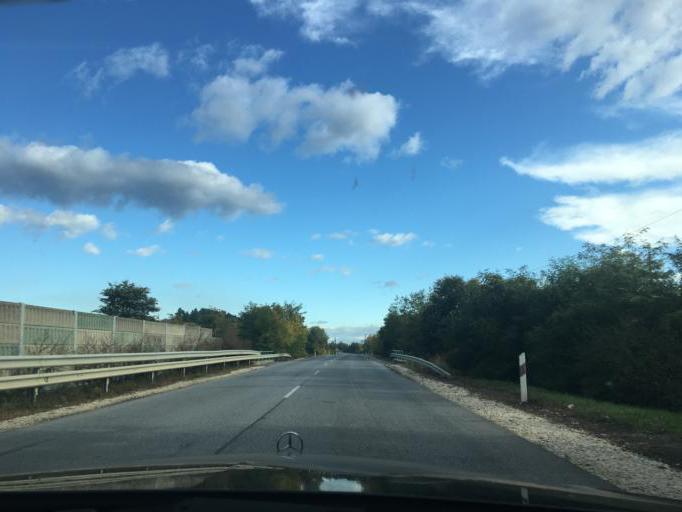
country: HU
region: Borsod-Abauj-Zemplen
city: Encs
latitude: 48.4009
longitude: 21.1673
